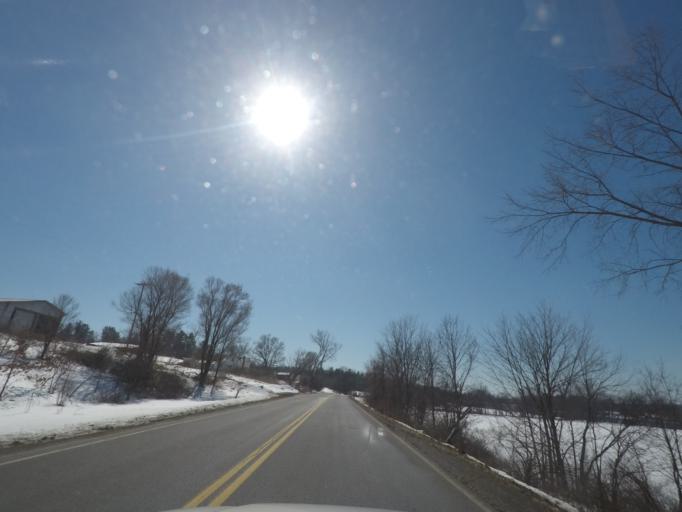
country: US
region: New York
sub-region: Saratoga County
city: Stillwater
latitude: 42.9888
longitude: -73.6036
